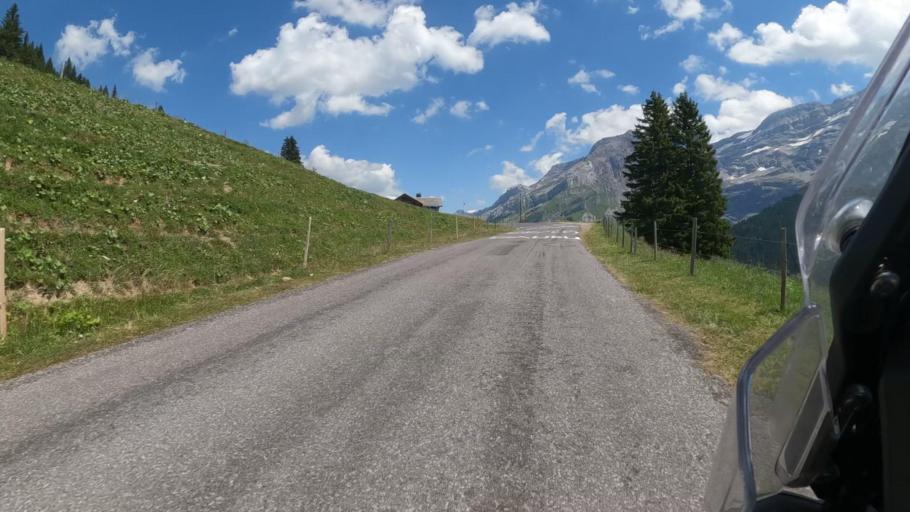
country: CH
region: Vaud
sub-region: Aigle District
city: Villars-sur-Ollon
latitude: 46.3308
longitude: 7.1365
